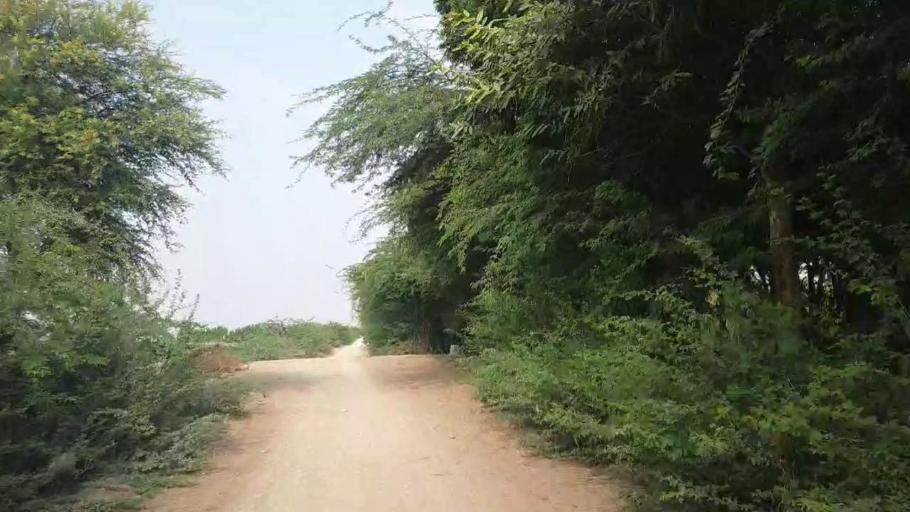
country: PK
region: Sindh
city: Badin
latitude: 24.5997
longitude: 68.7413
